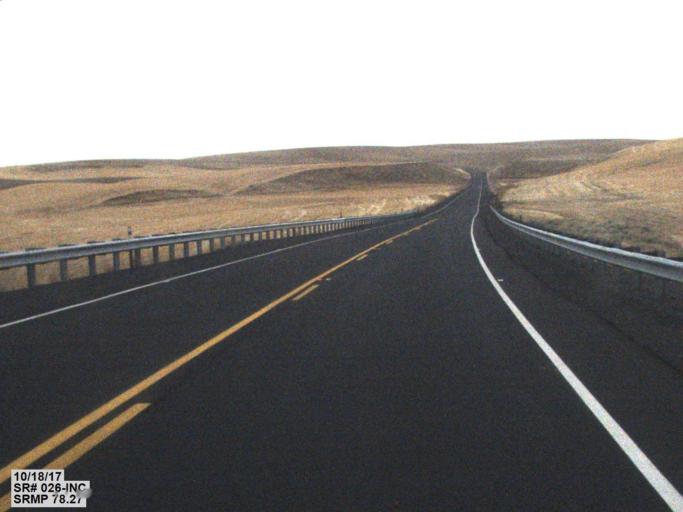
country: US
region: Washington
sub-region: Adams County
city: Ritzville
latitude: 46.7910
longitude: -118.3879
